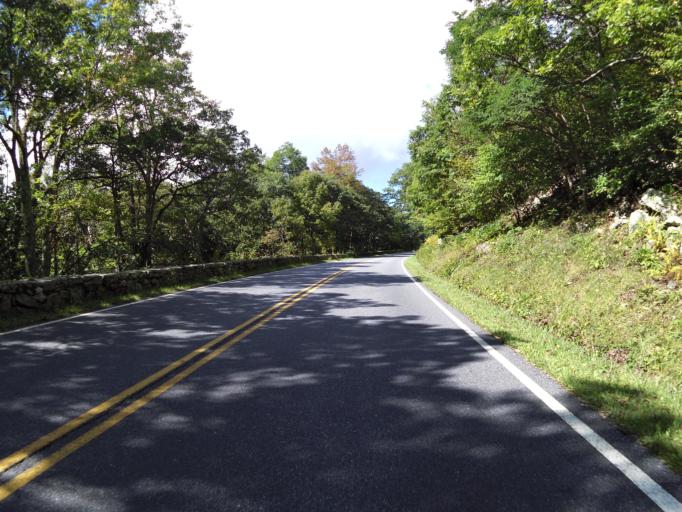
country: US
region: Virginia
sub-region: Page County
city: Luray
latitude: 38.5895
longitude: -78.3709
